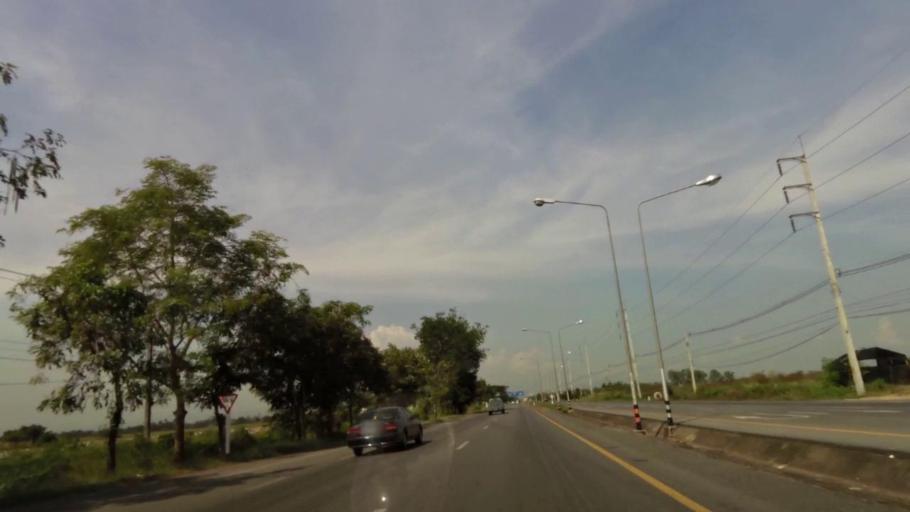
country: TH
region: Uttaradit
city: Uttaradit
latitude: 17.5670
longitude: 100.1562
